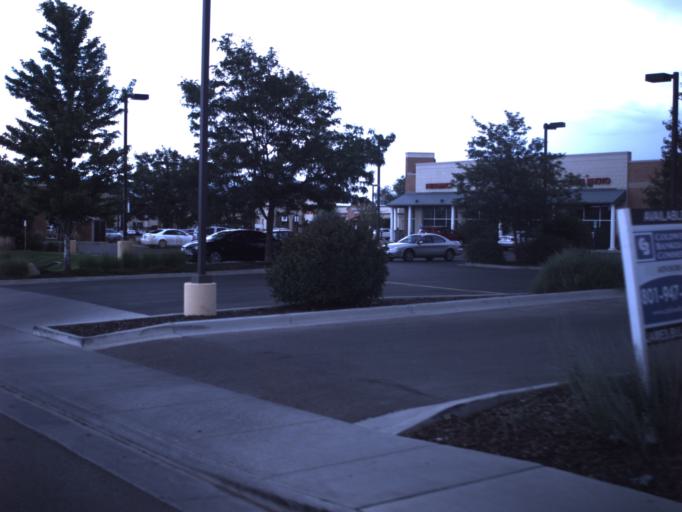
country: US
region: Utah
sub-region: Salt Lake County
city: Midvale
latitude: 40.6199
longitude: -111.8905
